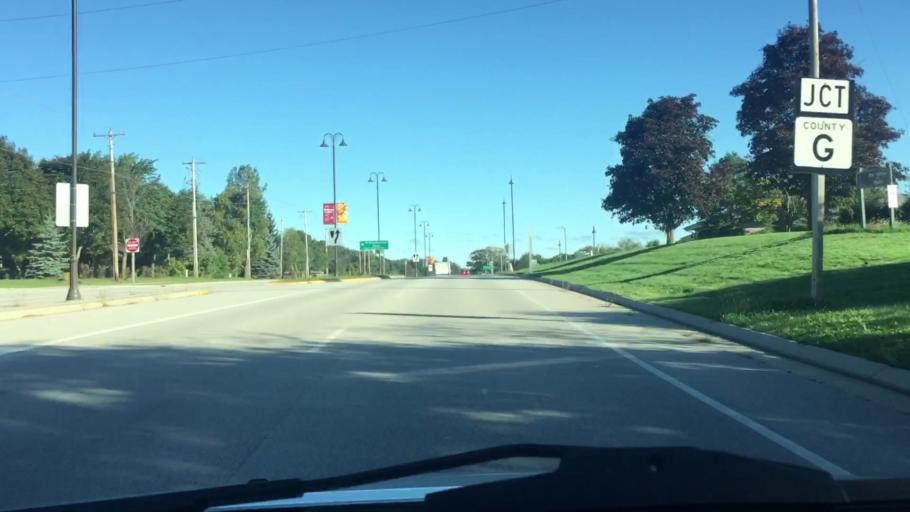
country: US
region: Wisconsin
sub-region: Waukesha County
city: Wales
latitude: 42.9930
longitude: -88.3842
